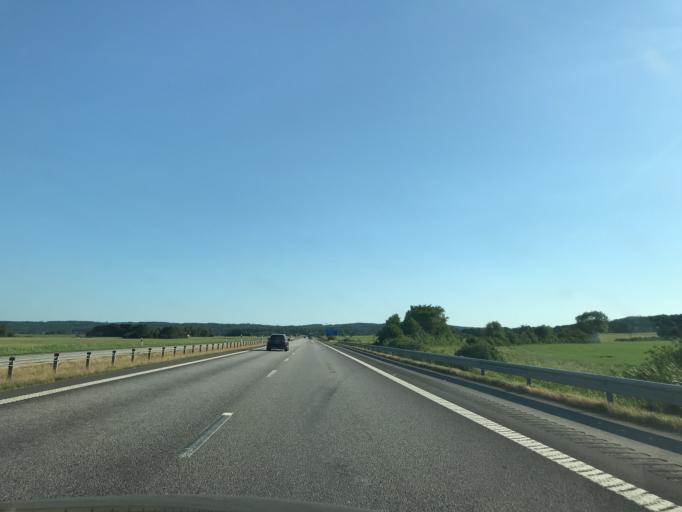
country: SE
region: Skane
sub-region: Angelholms Kommun
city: AEngelholm
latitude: 56.2995
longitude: 12.9060
